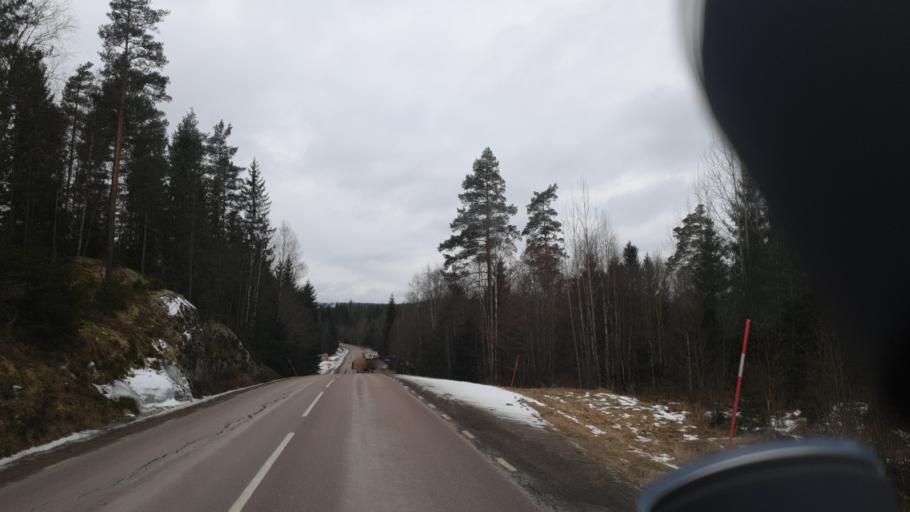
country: SE
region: Vaermland
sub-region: Eda Kommun
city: Charlottenberg
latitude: 59.8131
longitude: 12.1688
